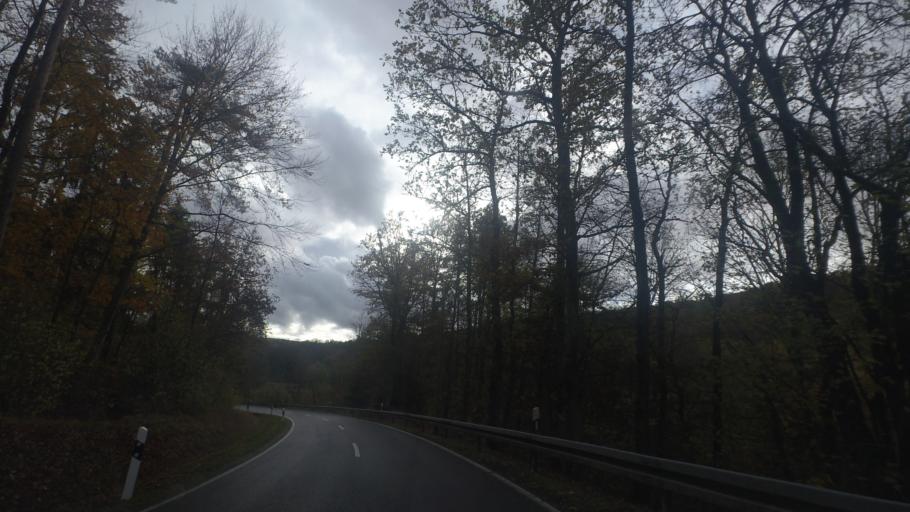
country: DE
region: Bavaria
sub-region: Regierungsbezirk Unterfranken
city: Aubstadt
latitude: 50.3505
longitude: 10.4137
